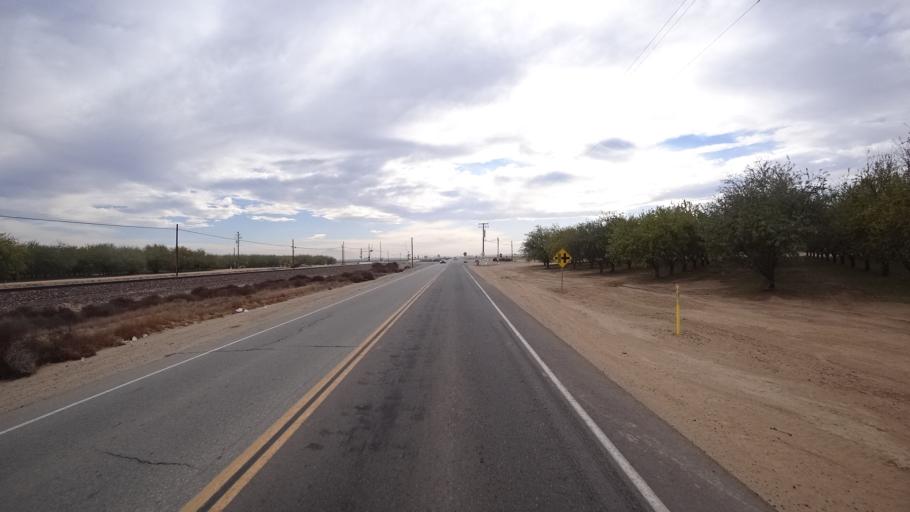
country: US
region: California
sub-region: Kern County
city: Rosedale
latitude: 35.4206
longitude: -119.1736
